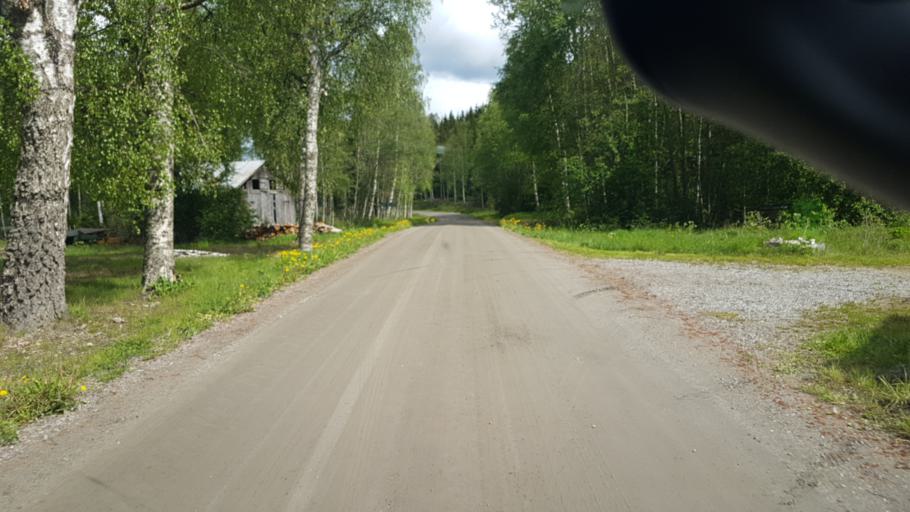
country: NO
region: Ostfold
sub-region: Romskog
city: Romskog
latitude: 59.6721
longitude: 11.9333
